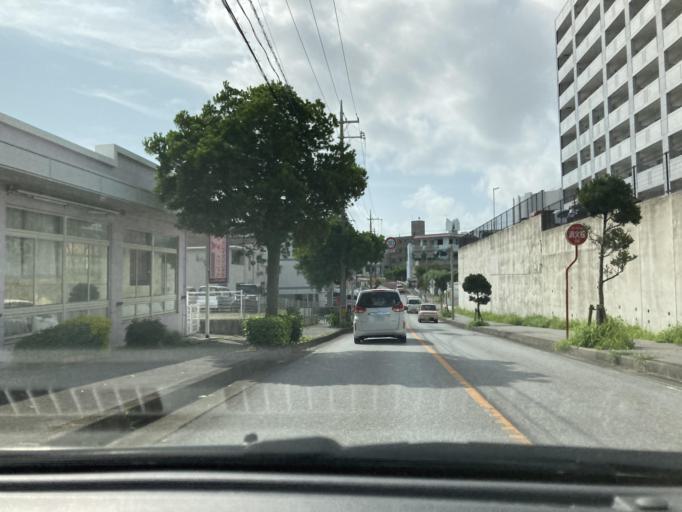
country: JP
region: Okinawa
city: Ginowan
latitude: 26.2577
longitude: 127.7687
